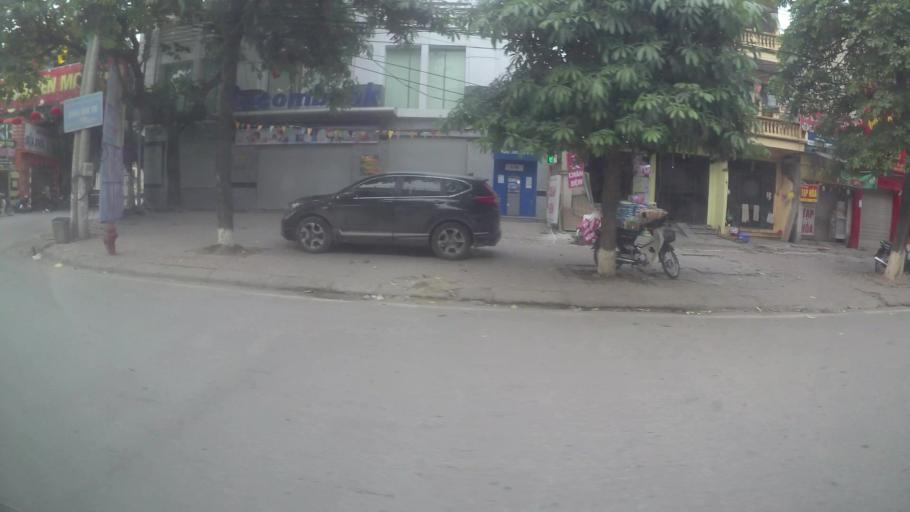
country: VN
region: Ha Noi
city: Cau Dien
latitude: 21.0458
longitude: 105.7508
